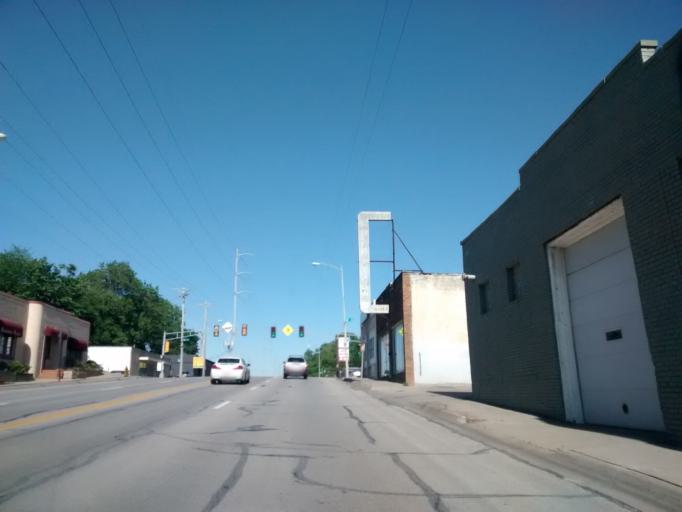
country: US
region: Nebraska
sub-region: Douglas County
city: Omaha
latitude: 41.2523
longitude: -95.9698
